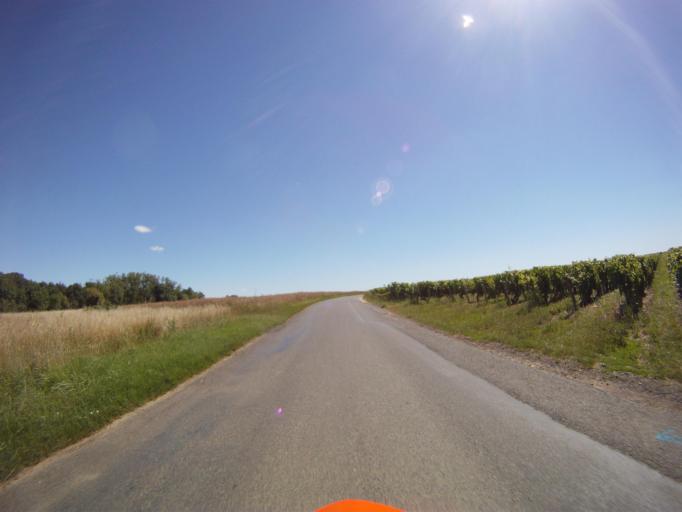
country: FR
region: Centre
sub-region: Departement d'Indre-et-Loire
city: Vouvray
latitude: 47.4421
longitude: 0.8001
